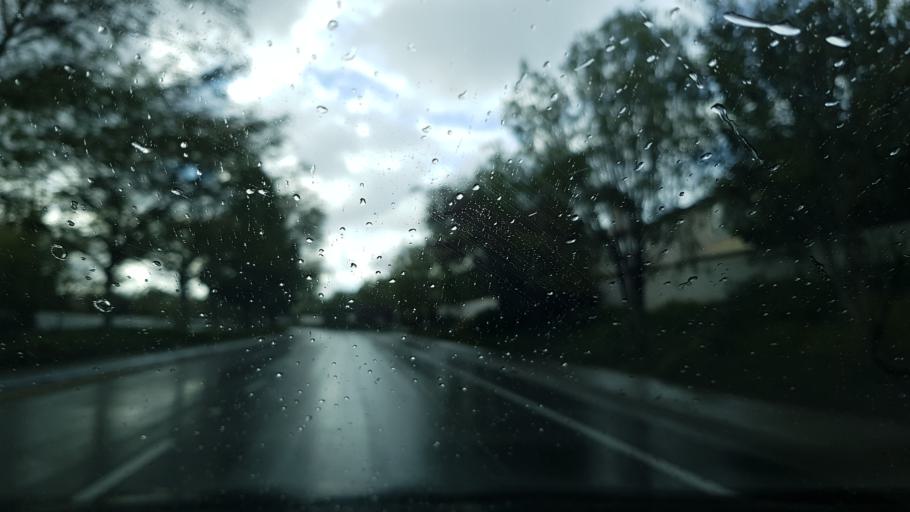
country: US
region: California
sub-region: San Diego County
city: Fairbanks Ranch
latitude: 32.9291
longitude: -117.1930
